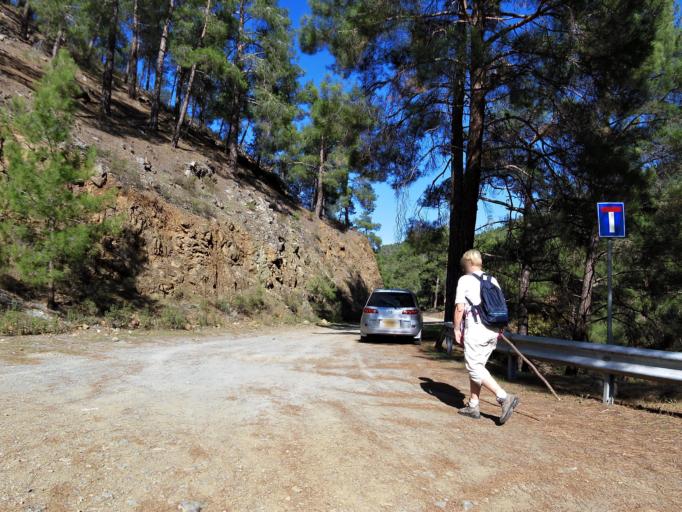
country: CY
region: Limassol
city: Kyperounta
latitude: 35.0000
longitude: 33.0375
